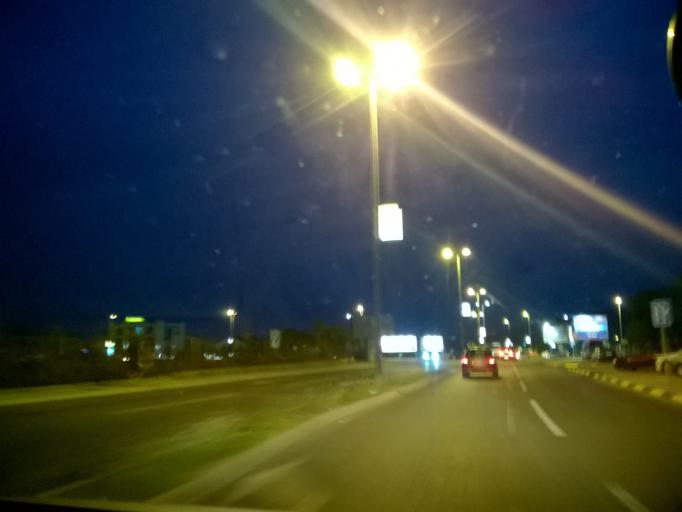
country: ME
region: Podgorica
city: Podgorica
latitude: 42.4360
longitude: 19.2275
